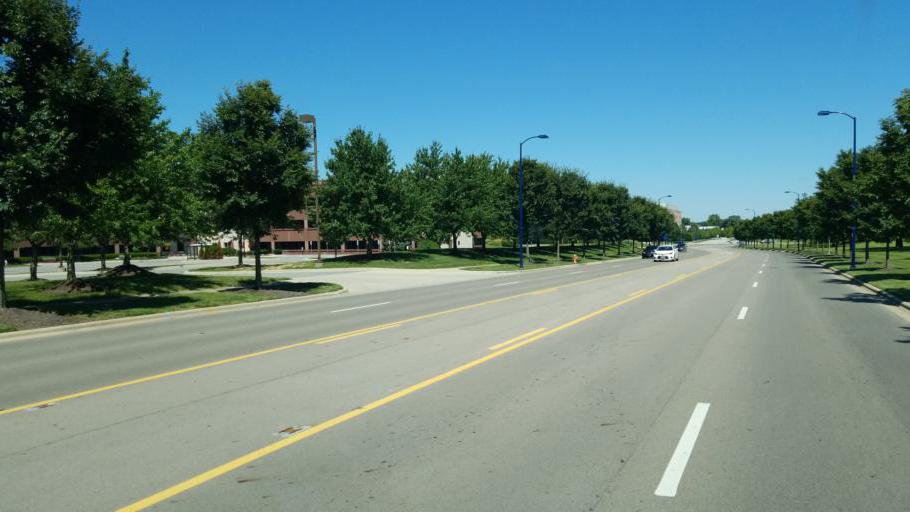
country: US
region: Ohio
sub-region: Franklin County
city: Gahanna
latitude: 40.0423
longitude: -82.9133
